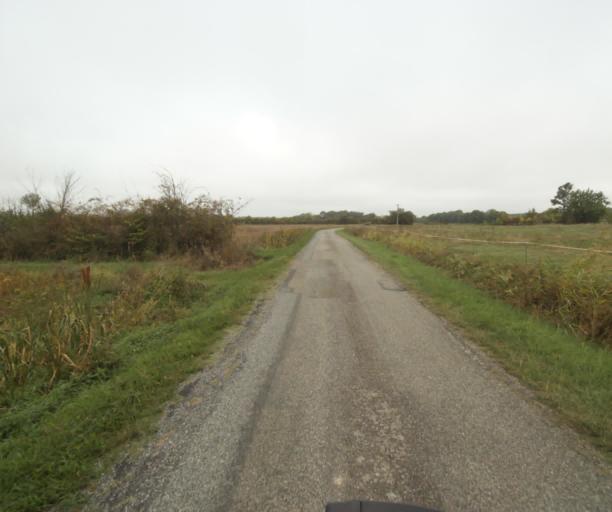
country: FR
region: Midi-Pyrenees
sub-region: Departement du Tarn-et-Garonne
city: Orgueil
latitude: 43.8994
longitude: 1.3865
